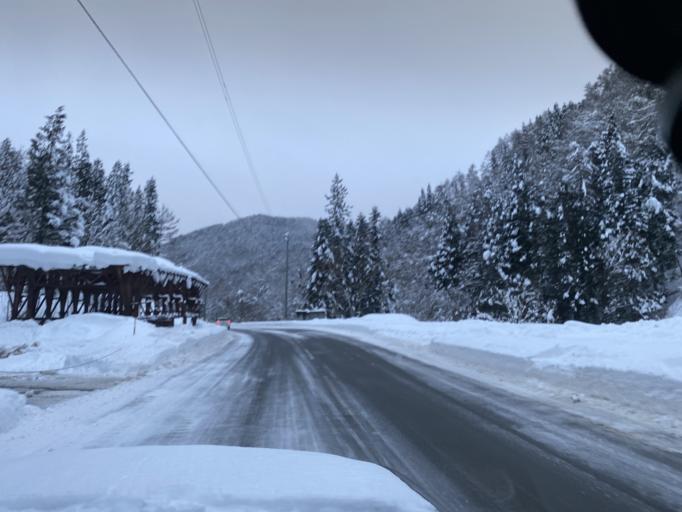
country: JP
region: Nagano
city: Omachi
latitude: 36.5996
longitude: 137.8885
